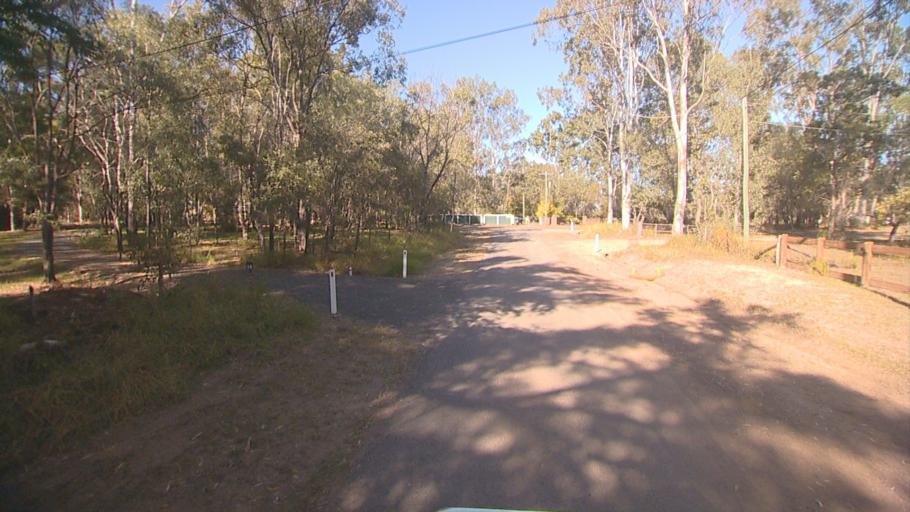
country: AU
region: Queensland
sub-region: Logan
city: Cedar Vale
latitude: -27.8440
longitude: 153.0401
